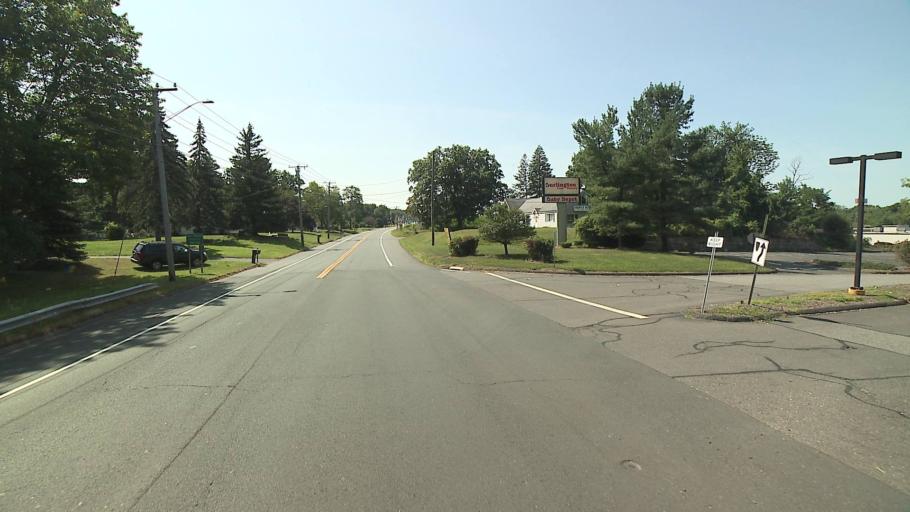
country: US
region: Connecticut
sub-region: Hartford County
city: Windsor Locks
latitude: 41.9366
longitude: -72.6039
